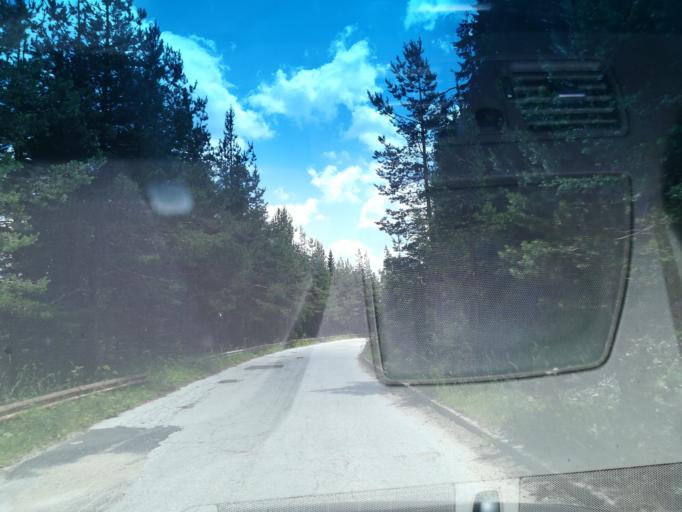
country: BG
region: Smolyan
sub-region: Obshtina Chepelare
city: Chepelare
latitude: 41.6886
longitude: 24.7577
